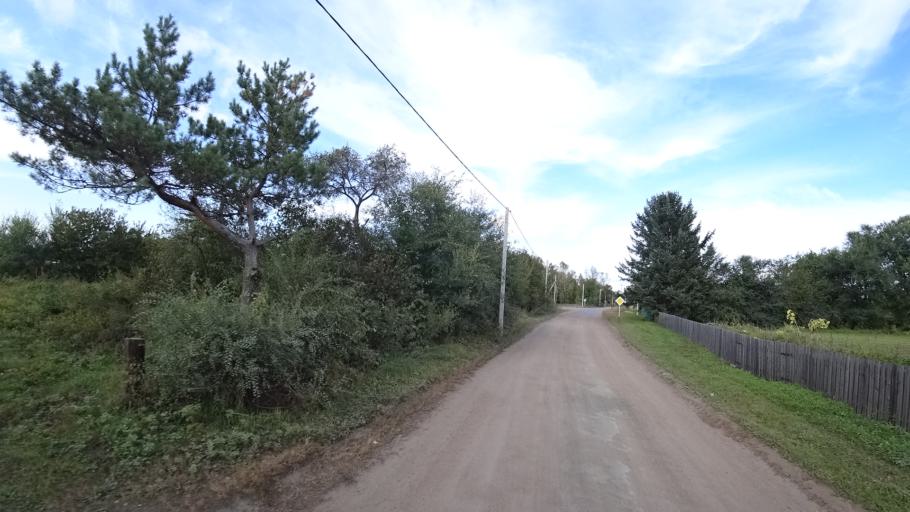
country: RU
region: Amur
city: Arkhara
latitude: 49.3588
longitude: 130.1166
